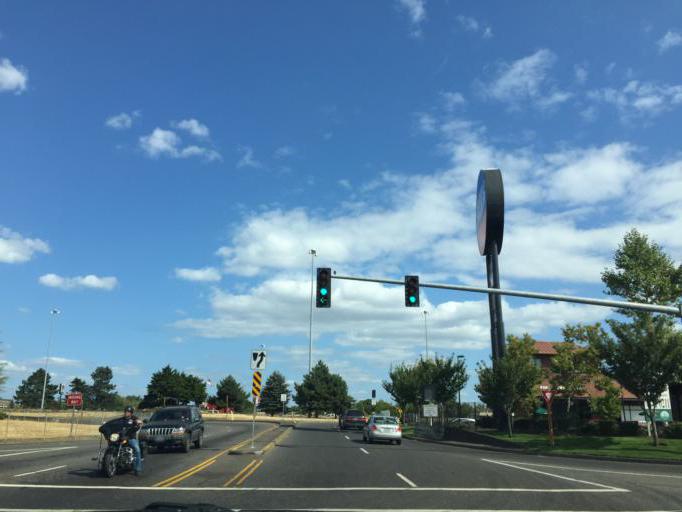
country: US
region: Washington
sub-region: Clark County
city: Vancouver
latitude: 45.6118
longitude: -122.6809
